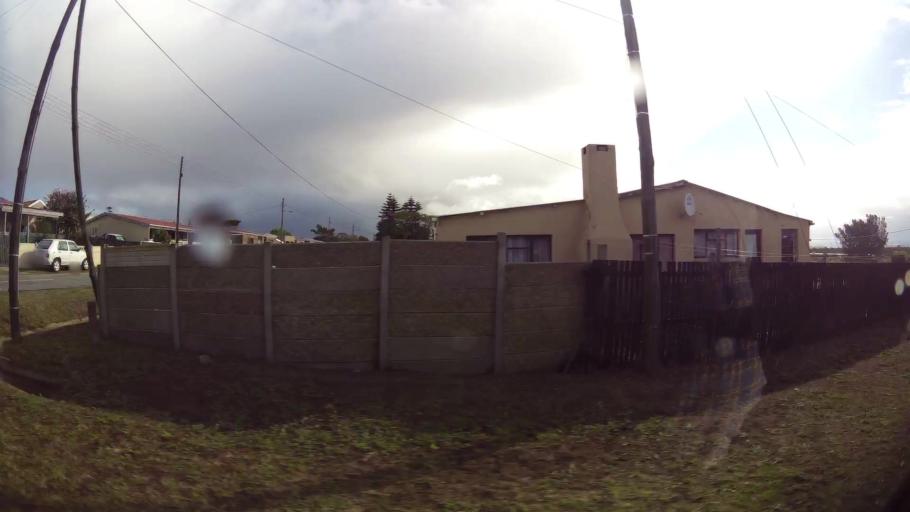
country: ZA
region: Western Cape
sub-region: Eden District Municipality
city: Mossel Bay
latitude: -34.1865
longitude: 22.1227
